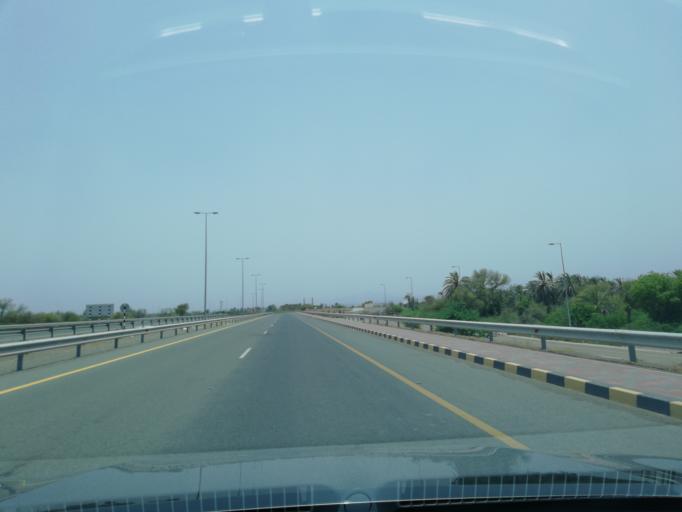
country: OM
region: Al Batinah
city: Shinas
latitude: 24.7402
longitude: 56.4577
